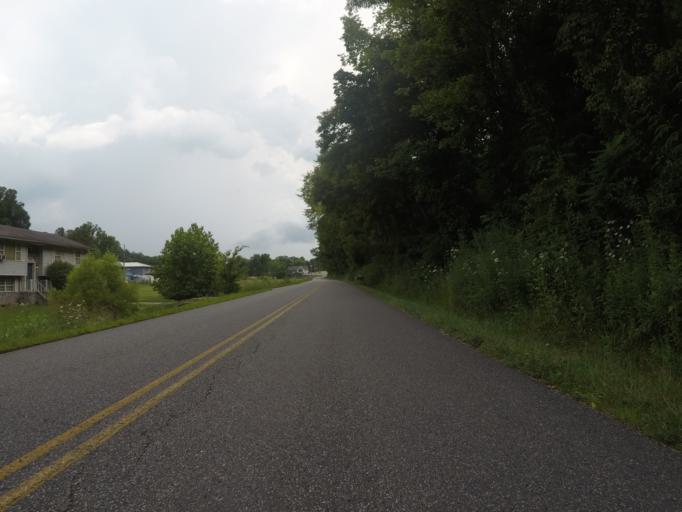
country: US
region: Kentucky
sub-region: Boyd County
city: Meads
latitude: 38.4283
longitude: -82.7085
